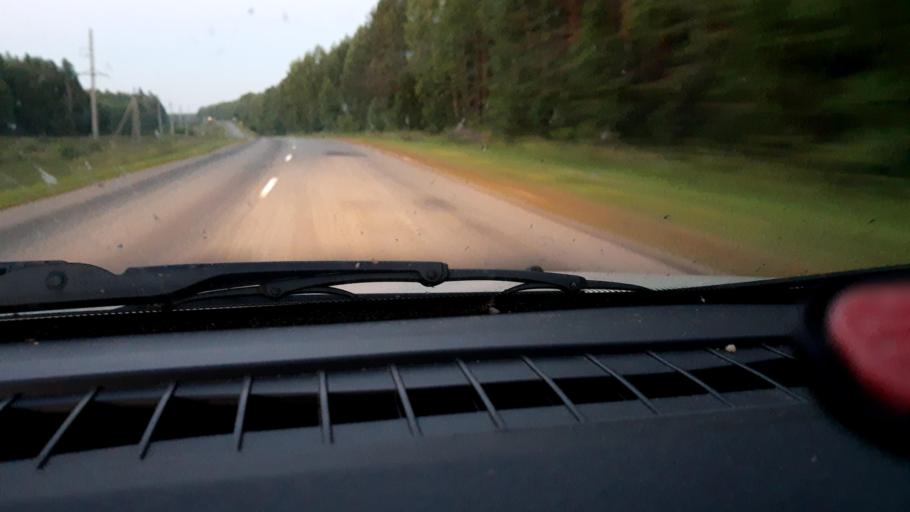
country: RU
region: Nizjnij Novgorod
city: Prudy
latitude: 57.3611
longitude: 46.1907
